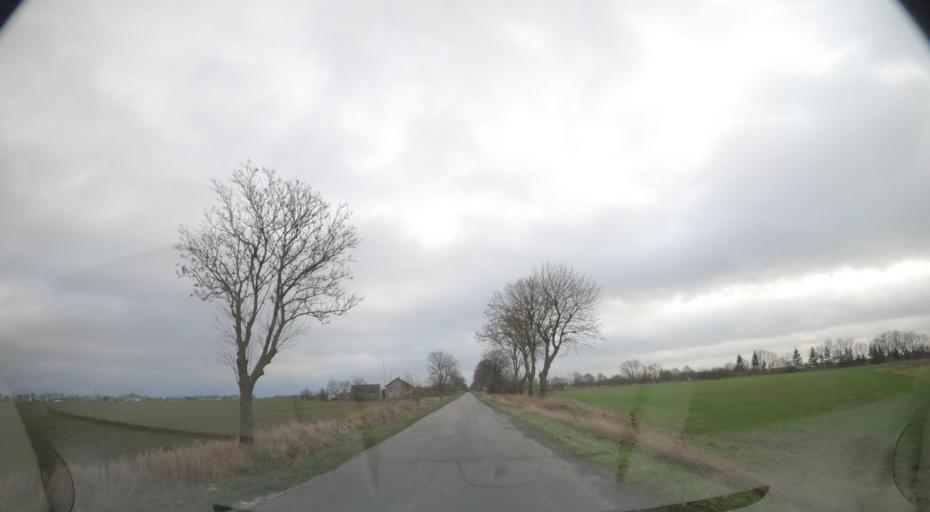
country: PL
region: Greater Poland Voivodeship
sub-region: Powiat pilski
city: Lobzenica
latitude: 53.2617
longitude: 17.2307
